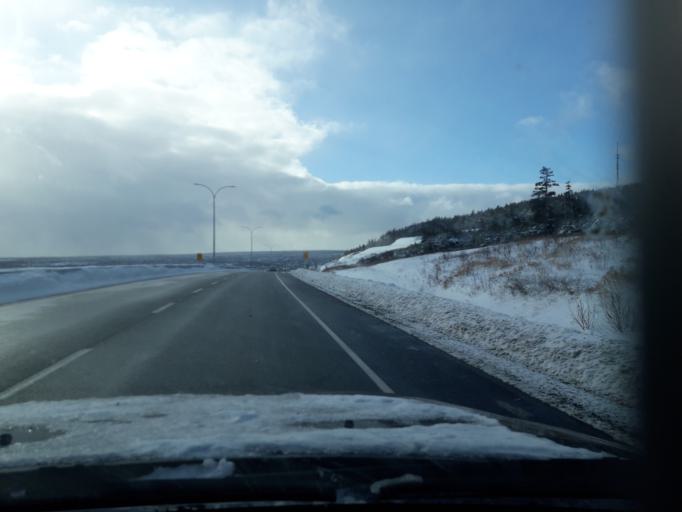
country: CA
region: Newfoundland and Labrador
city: Mount Pearl
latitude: 47.5361
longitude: -52.7759
